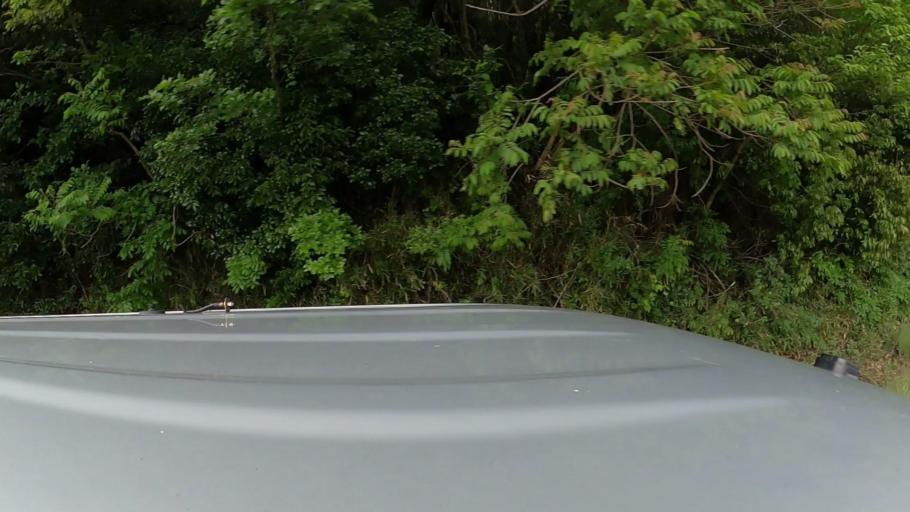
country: JP
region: Ibaraki
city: Ushiku
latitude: 35.9655
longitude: 140.2001
